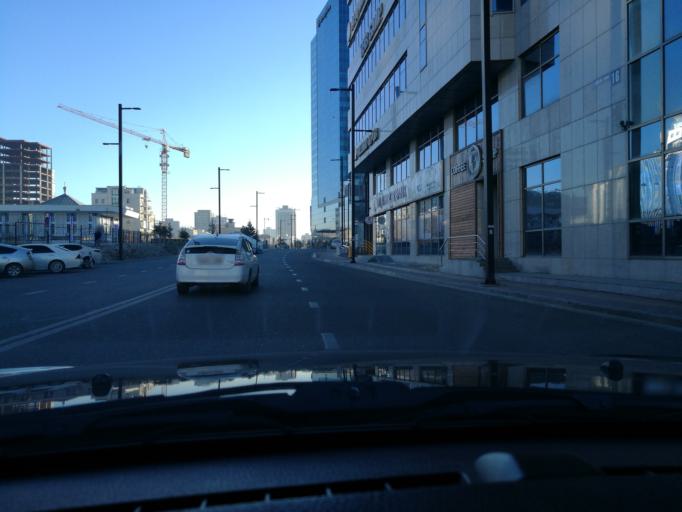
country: MN
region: Ulaanbaatar
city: Ulaanbaatar
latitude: 47.9134
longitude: 106.9179
